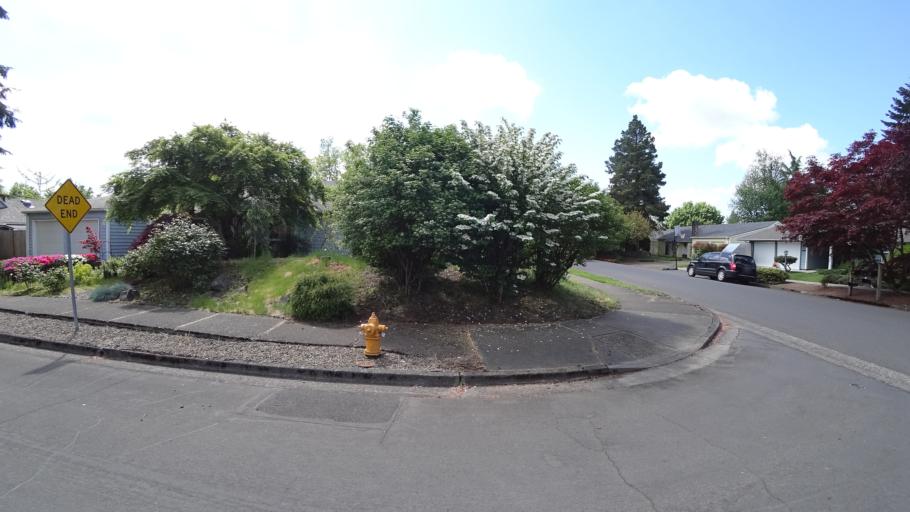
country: US
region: Oregon
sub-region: Washington County
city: Aloha
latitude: 45.5019
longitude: -122.8859
